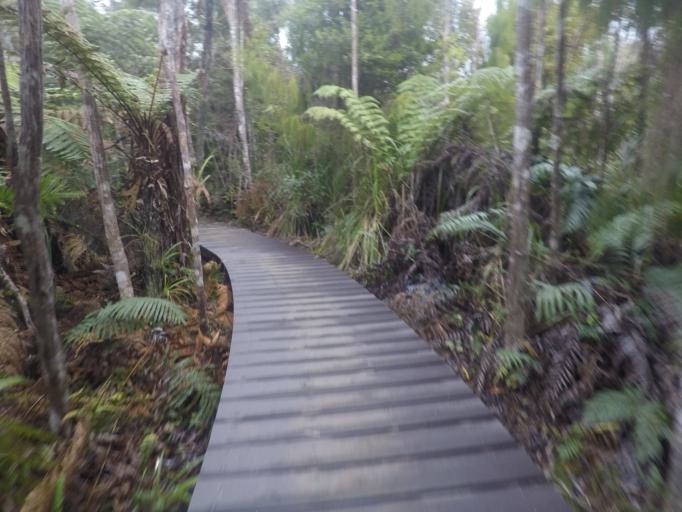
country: NZ
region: Auckland
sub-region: Auckland
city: Titirangi
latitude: -37.0017
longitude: 174.5392
